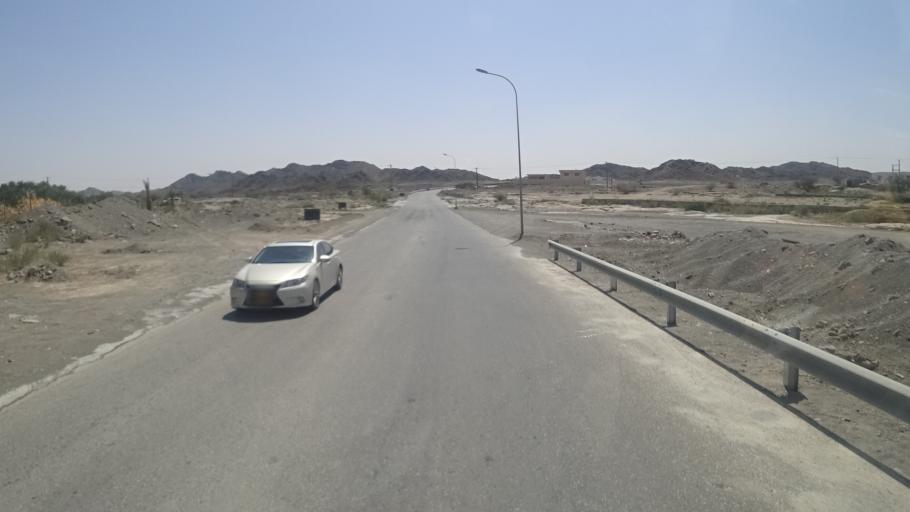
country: OM
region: Ash Sharqiyah
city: Ibra'
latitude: 22.6791
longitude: 58.5342
